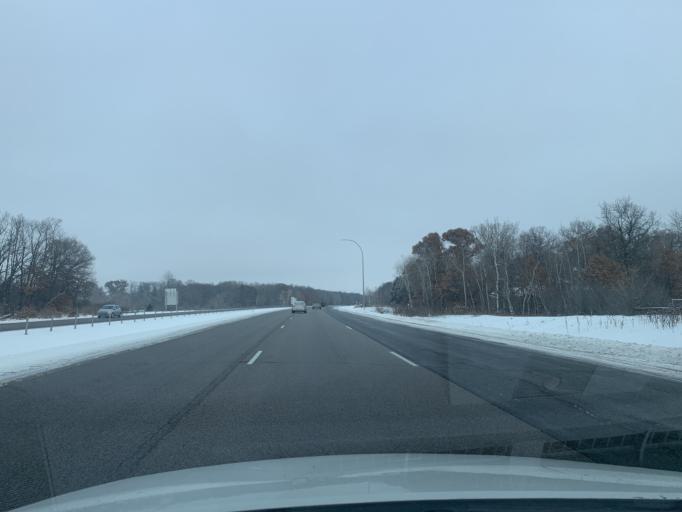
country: US
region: Minnesota
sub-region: Chisago County
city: Stacy
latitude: 45.3998
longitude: -92.9948
